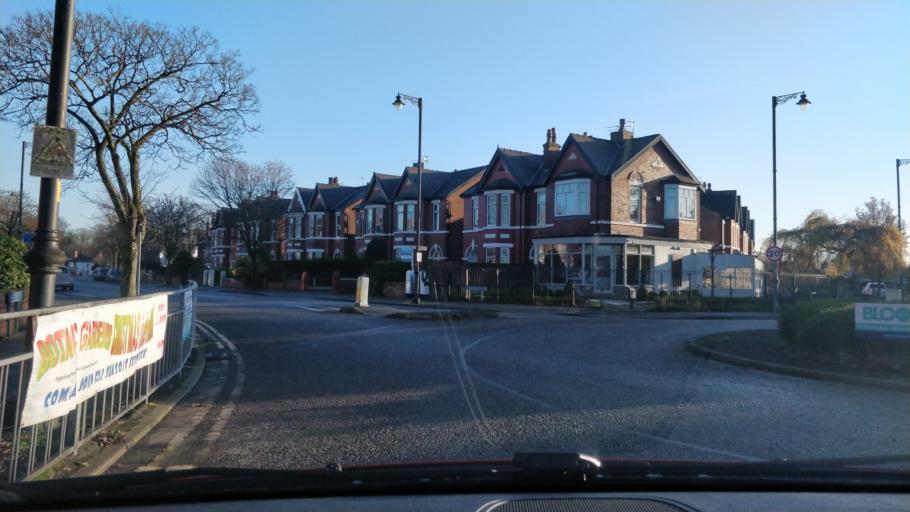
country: GB
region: England
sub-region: Sefton
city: Southport
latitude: 53.6607
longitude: -2.9655
